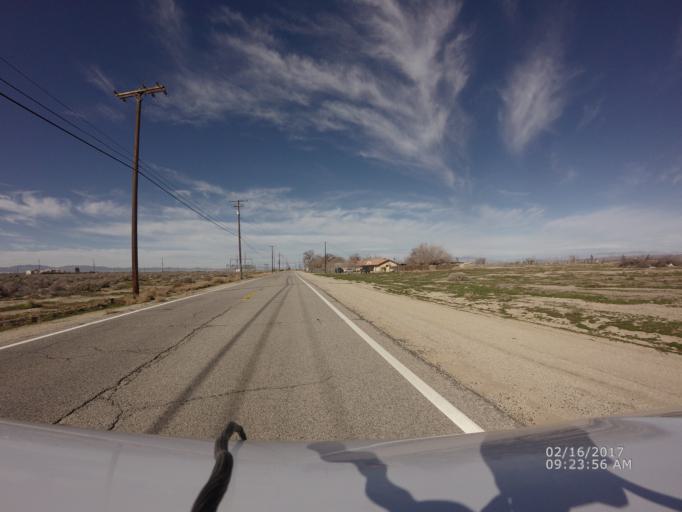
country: US
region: California
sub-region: Kern County
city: Edwards Air Force Base
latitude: 34.7637
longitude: -117.9662
